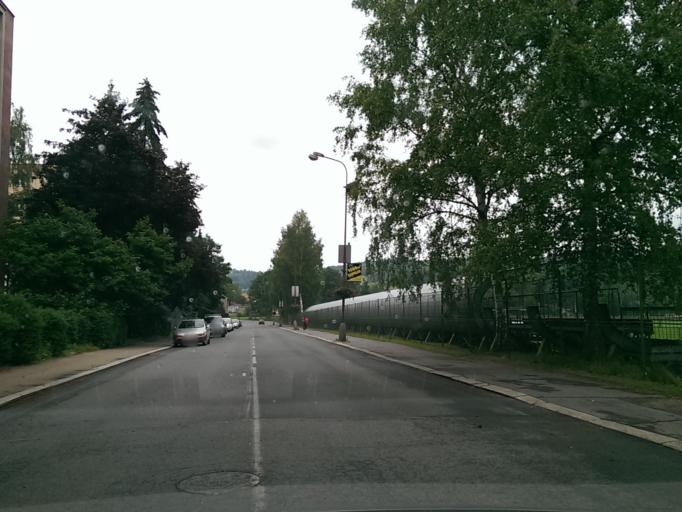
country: CZ
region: Liberecky
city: Semily
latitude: 50.6033
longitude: 15.3288
